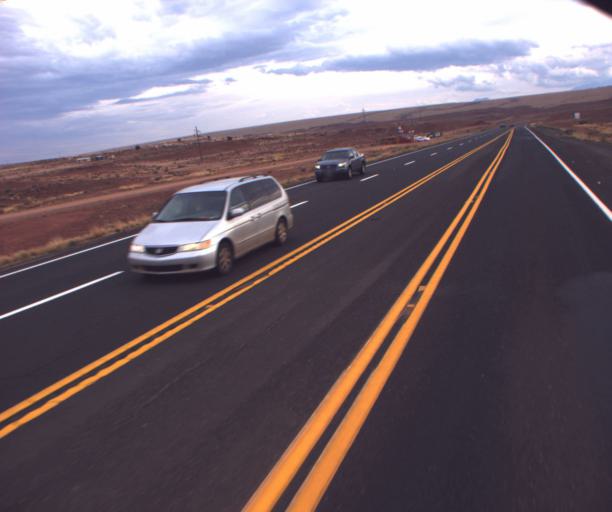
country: US
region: Arizona
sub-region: Coconino County
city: Tuba City
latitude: 35.7968
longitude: -111.4478
